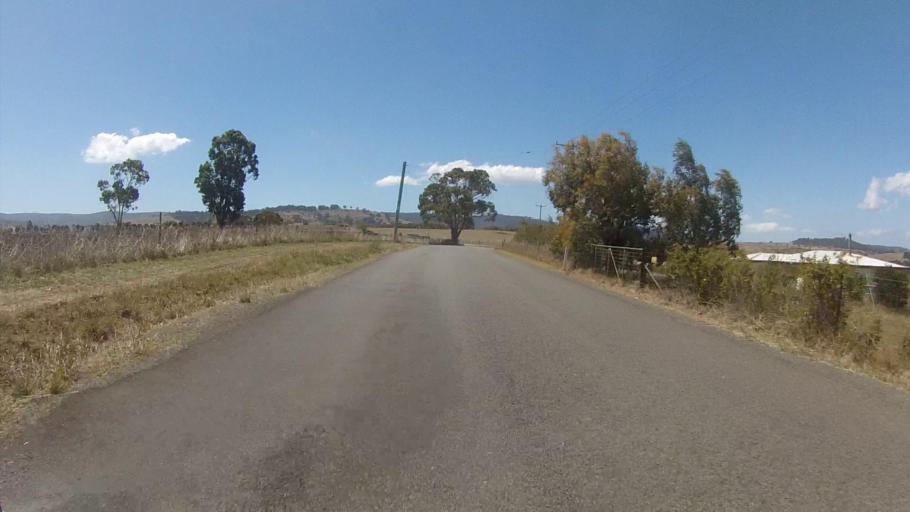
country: AU
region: Tasmania
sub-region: Sorell
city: Sorell
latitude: -42.7741
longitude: 147.5817
